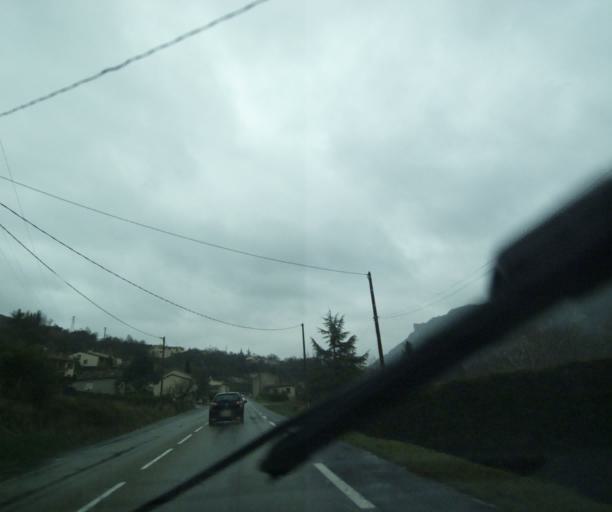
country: FR
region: Rhone-Alpes
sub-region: Departement de l'Ardeche
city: Flaviac
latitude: 44.7418
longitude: 4.6603
